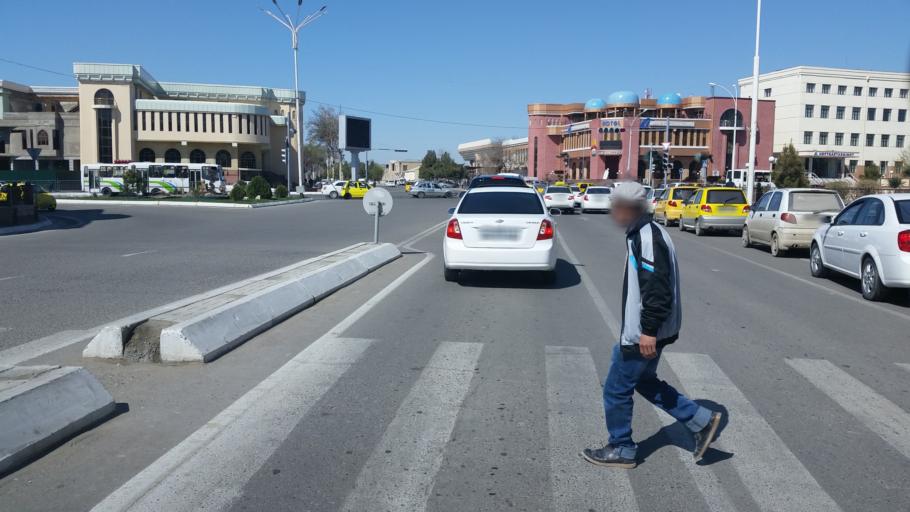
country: UZ
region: Bukhara
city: Bukhara
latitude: 39.7734
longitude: 64.4325
